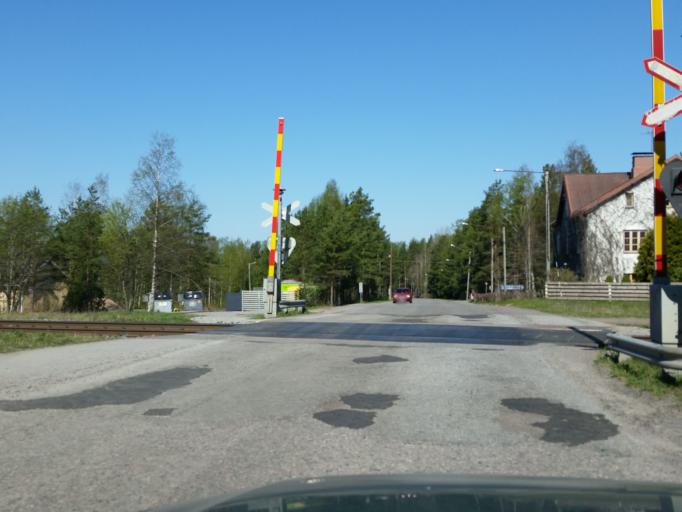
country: FI
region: Uusimaa
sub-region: Raaseporin
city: Inga
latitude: 60.1383
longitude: 23.8626
